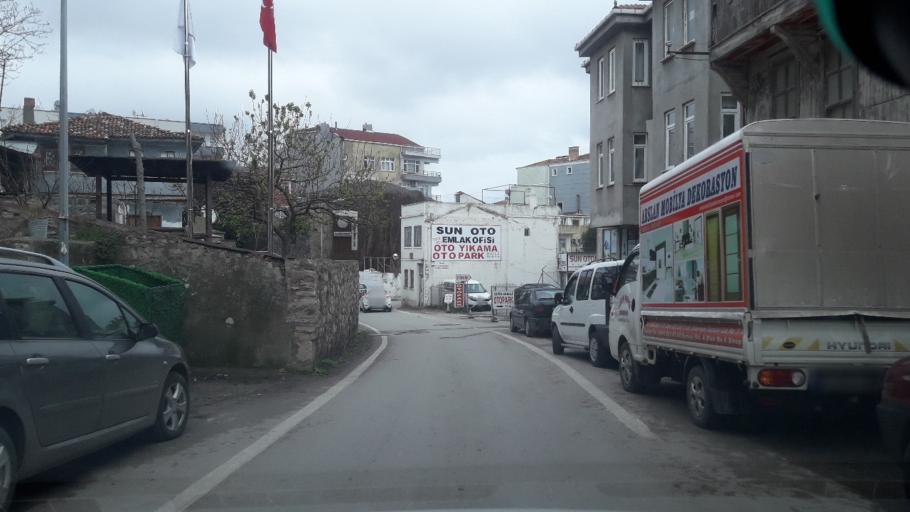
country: TR
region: Sinop
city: Sinop
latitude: 42.0252
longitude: 35.1452
